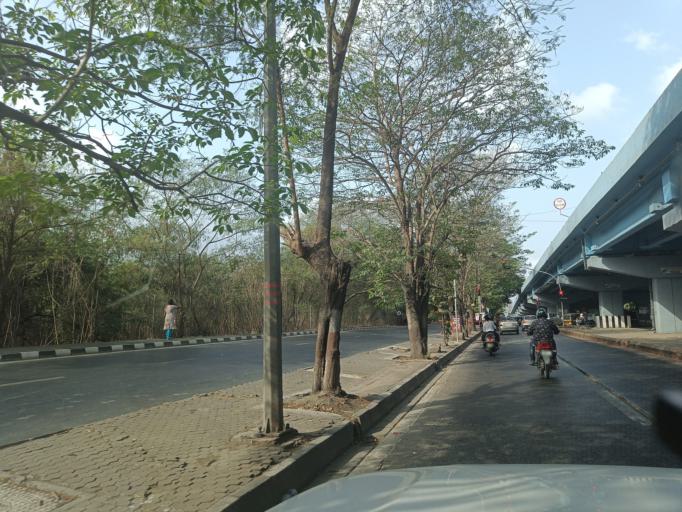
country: IN
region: Maharashtra
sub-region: Mumbai Suburban
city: Powai
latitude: 19.0846
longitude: 72.9216
